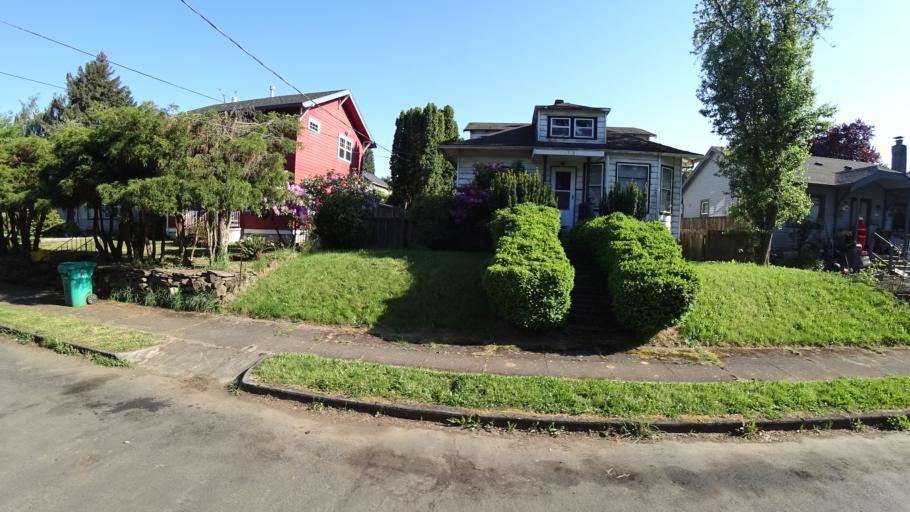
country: US
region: Oregon
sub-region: Multnomah County
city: Portland
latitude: 45.5554
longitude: -122.6871
